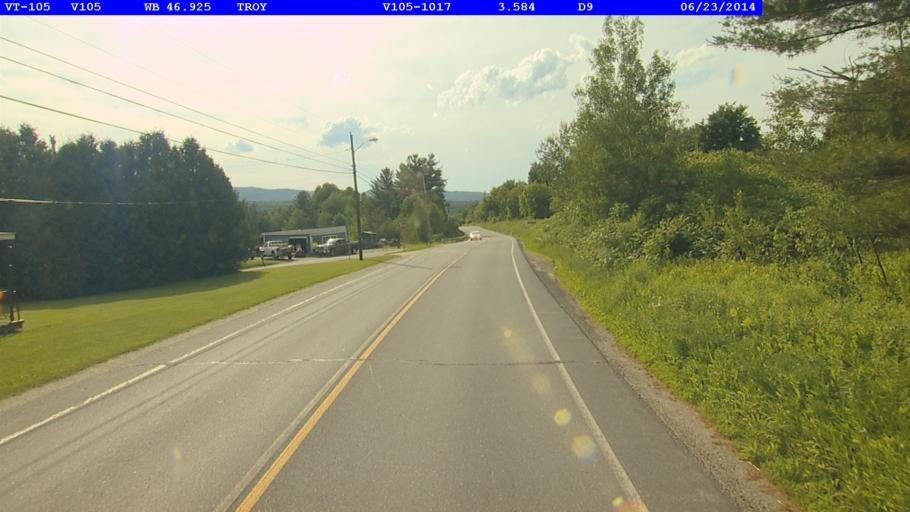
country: US
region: Vermont
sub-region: Orleans County
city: Newport
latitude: 44.9922
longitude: -72.3861
